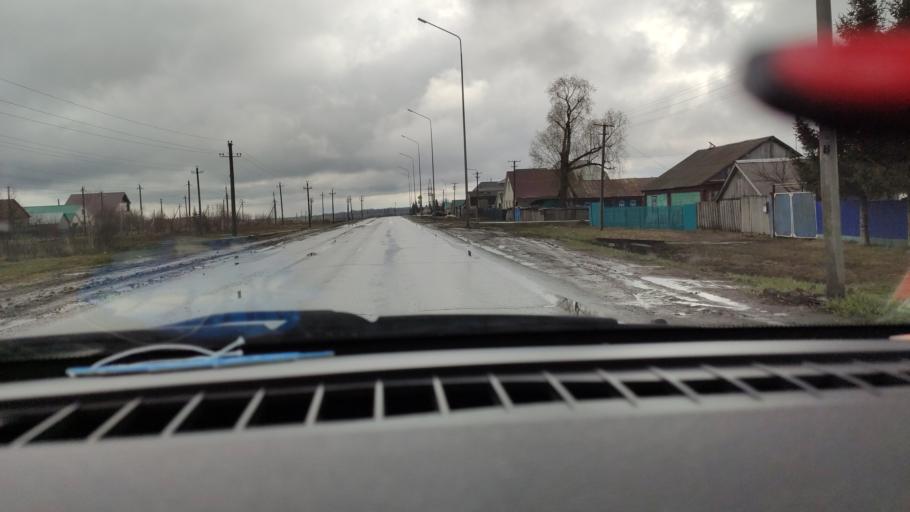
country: RU
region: Tatarstan
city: Nurlat
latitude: 54.4319
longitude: 50.8265
